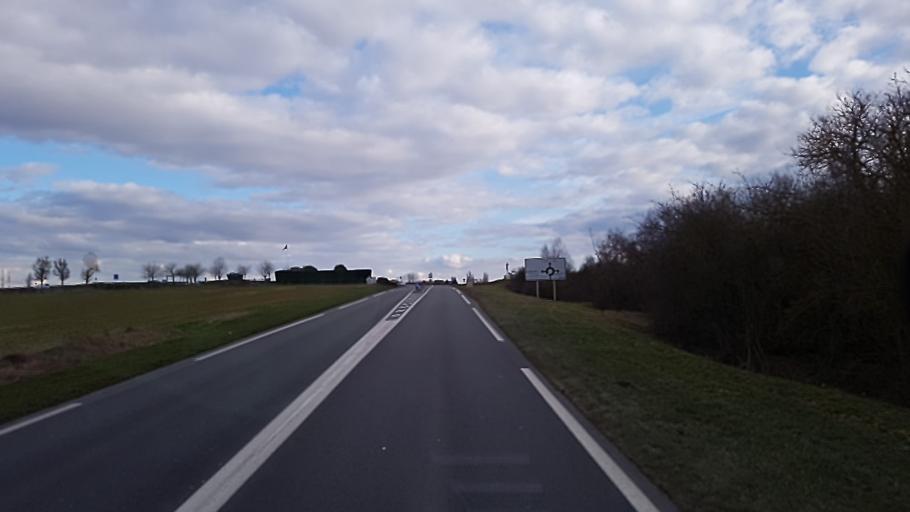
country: FR
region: Champagne-Ardenne
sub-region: Departement de la Marne
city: Cormicy
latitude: 49.4142
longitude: 3.8848
